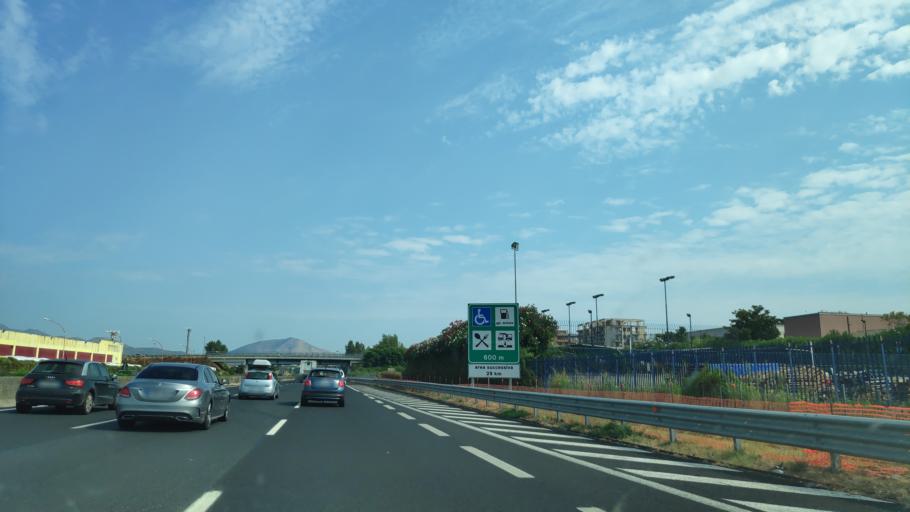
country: IT
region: Campania
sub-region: Provincia di Caserta
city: Capodrise
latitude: 41.0416
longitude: 14.3227
